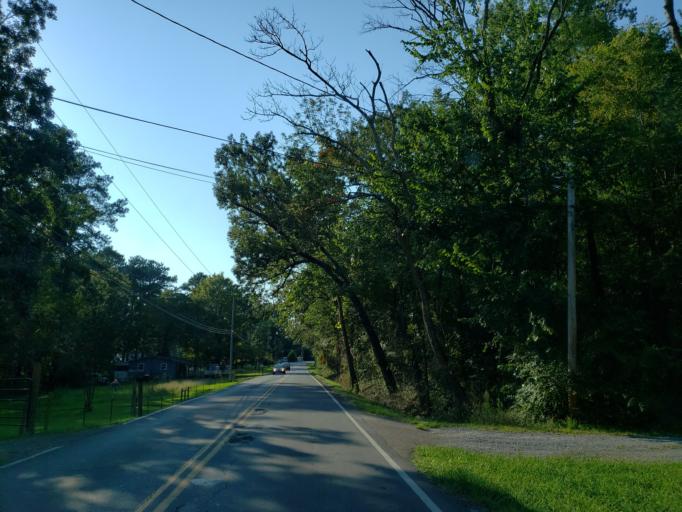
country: US
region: Tennessee
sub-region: Bradley County
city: Wildwood Lake
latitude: 35.1057
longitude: -84.8200
